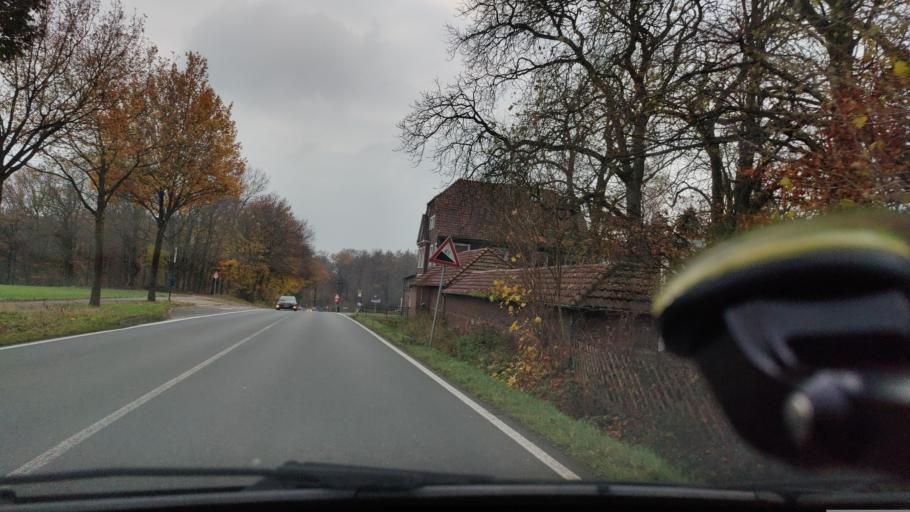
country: DE
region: North Rhine-Westphalia
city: Lunen
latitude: 51.6480
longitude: 7.5065
